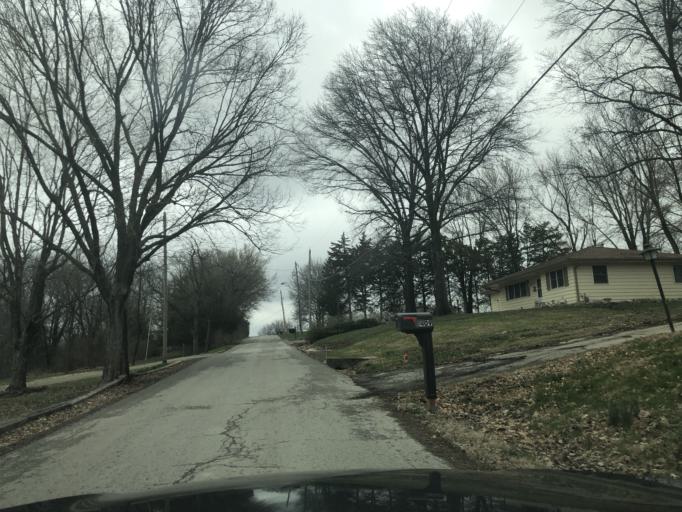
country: US
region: Kansas
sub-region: Leavenworth County
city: Lansing
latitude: 39.2748
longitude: -94.9138
